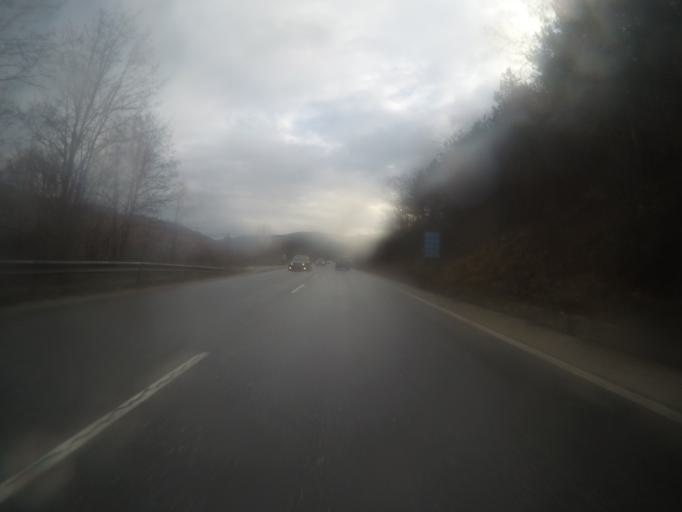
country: BG
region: Blagoevgrad
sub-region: Obshtina Simitli
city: Simitli
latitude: 41.8795
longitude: 23.1375
